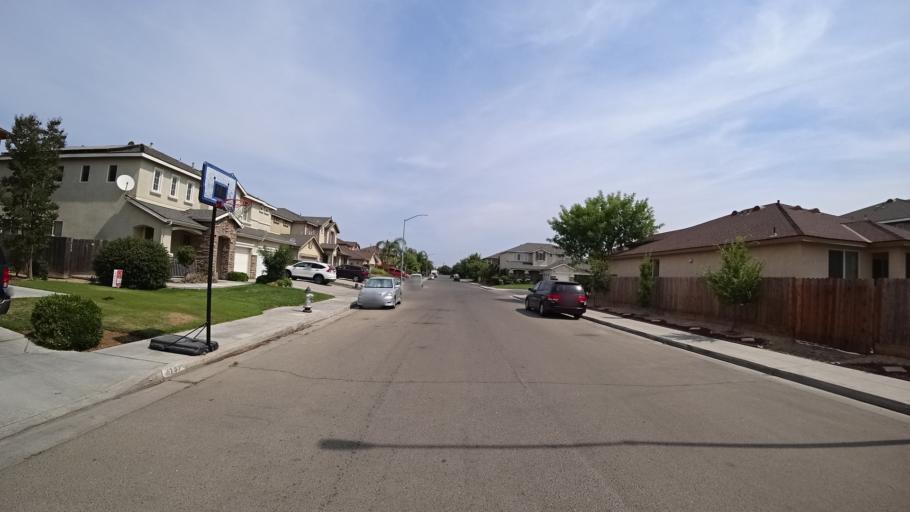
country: US
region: California
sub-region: Fresno County
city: West Park
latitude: 36.7616
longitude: -119.8776
